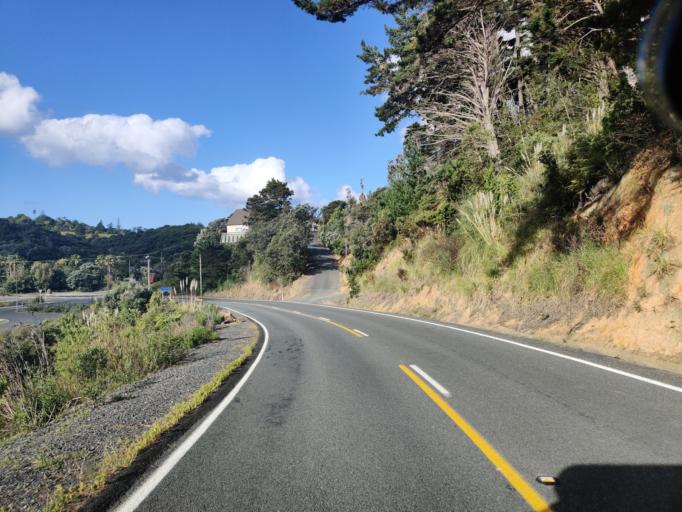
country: NZ
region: Northland
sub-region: Whangarei
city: Ngunguru
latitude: -35.6120
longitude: 174.5239
